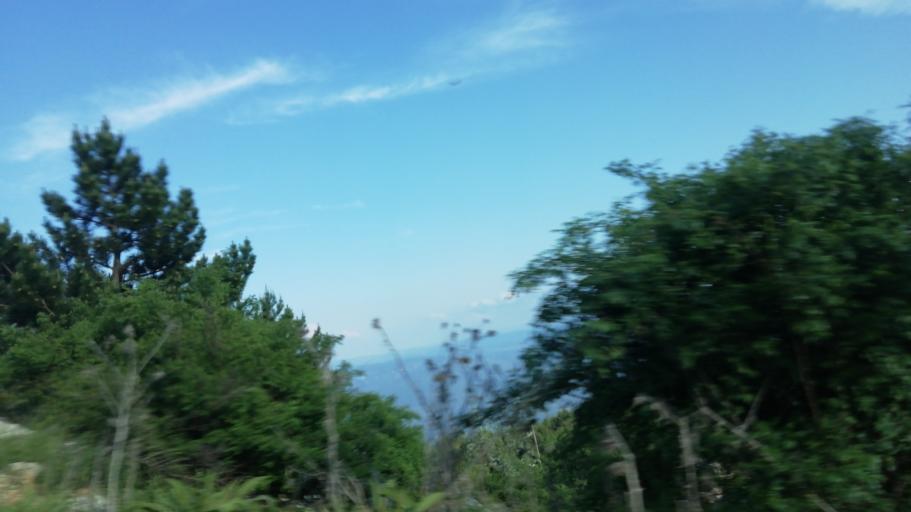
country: TR
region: Karabuk
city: Eskipazar
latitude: 41.0486
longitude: 32.5607
